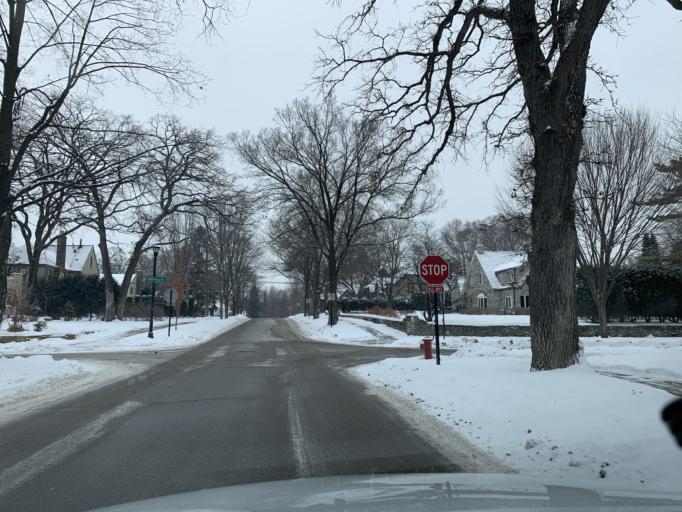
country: US
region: Minnesota
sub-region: Hennepin County
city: Edina
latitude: 44.9181
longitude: -93.3443
